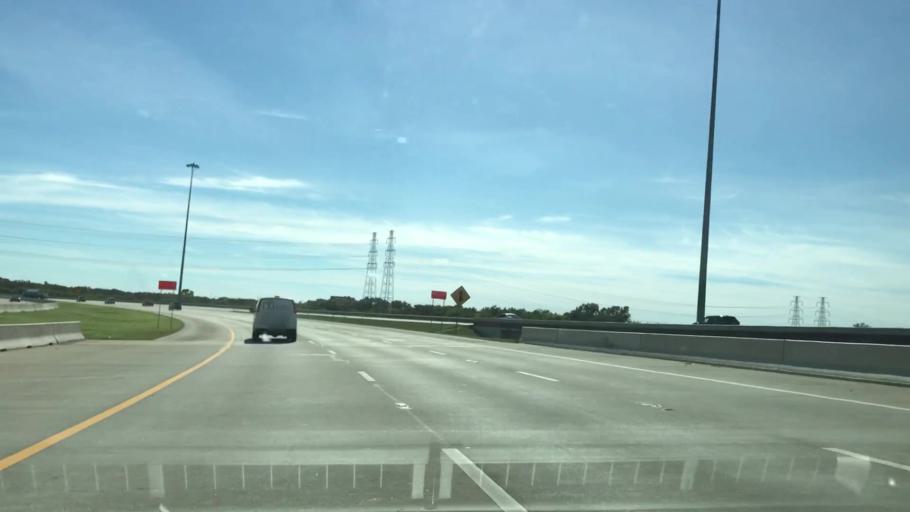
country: US
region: Texas
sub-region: Dallas County
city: Carrollton
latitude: 32.9795
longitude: -96.9336
